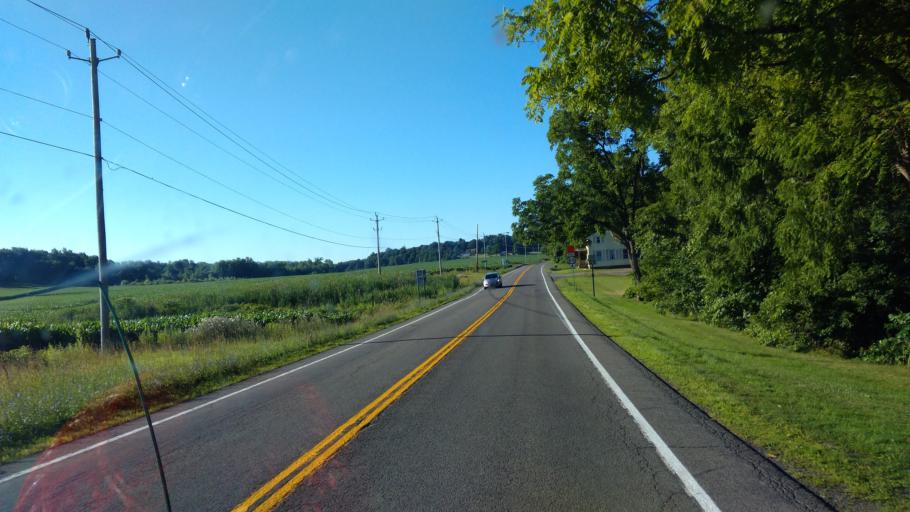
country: US
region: New York
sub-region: Wayne County
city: Lyons
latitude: 43.0214
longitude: -76.9874
